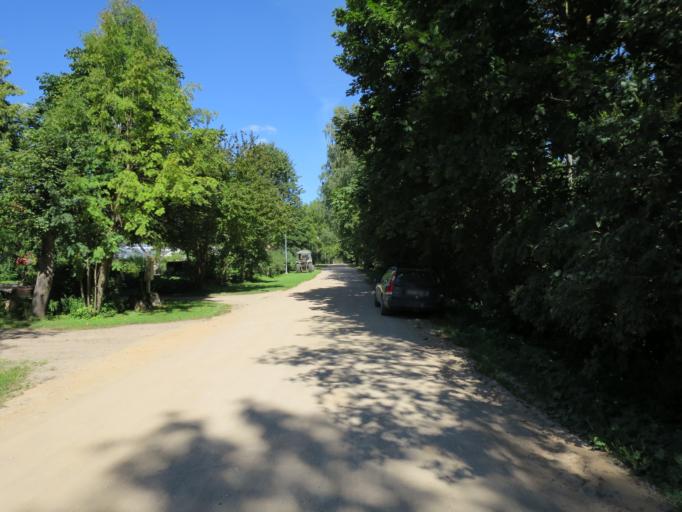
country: LV
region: Malpils
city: Malpils
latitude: 57.0085
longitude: 24.9664
